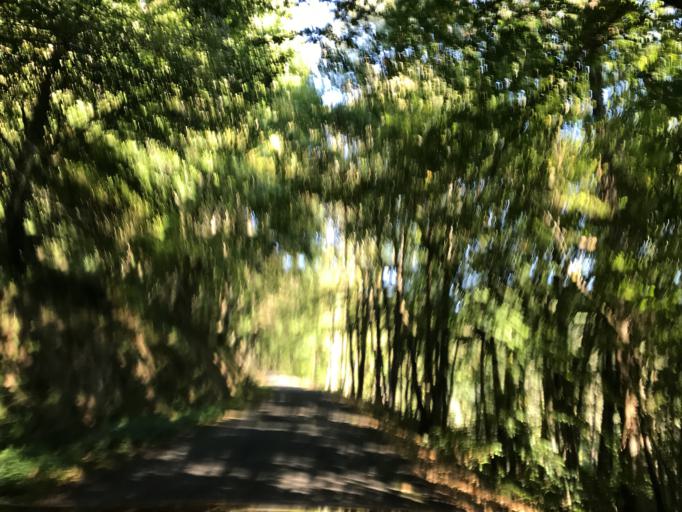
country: FR
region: Auvergne
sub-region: Departement du Puy-de-Dome
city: Escoutoux
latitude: 45.7761
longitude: 3.6103
